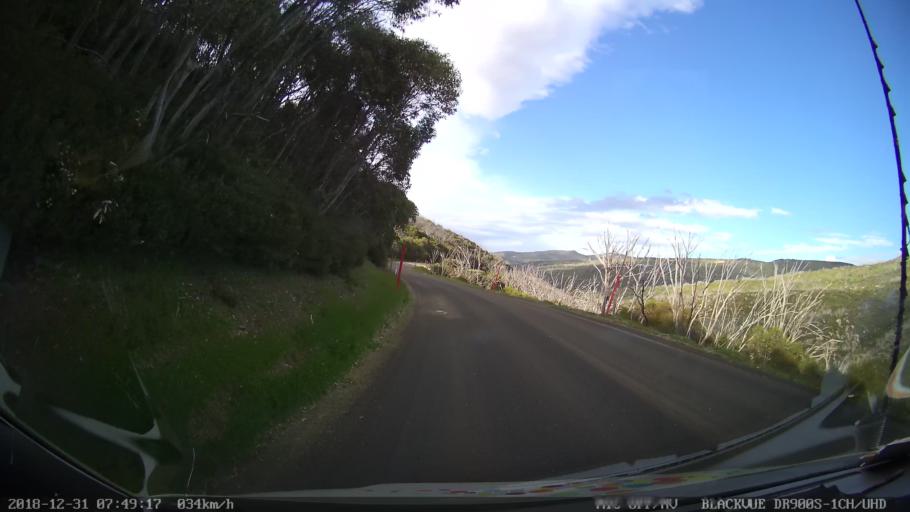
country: AU
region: New South Wales
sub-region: Snowy River
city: Jindabyne
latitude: -36.3704
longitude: 148.3865
